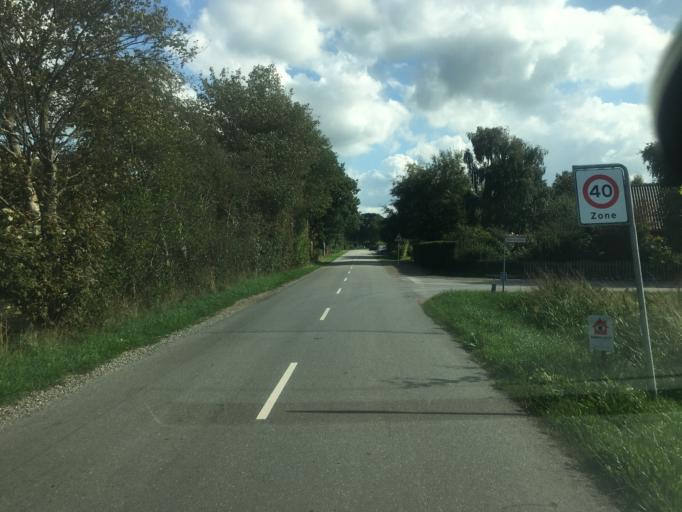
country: DE
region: Schleswig-Holstein
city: Ellhoft
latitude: 54.9502
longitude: 8.9641
